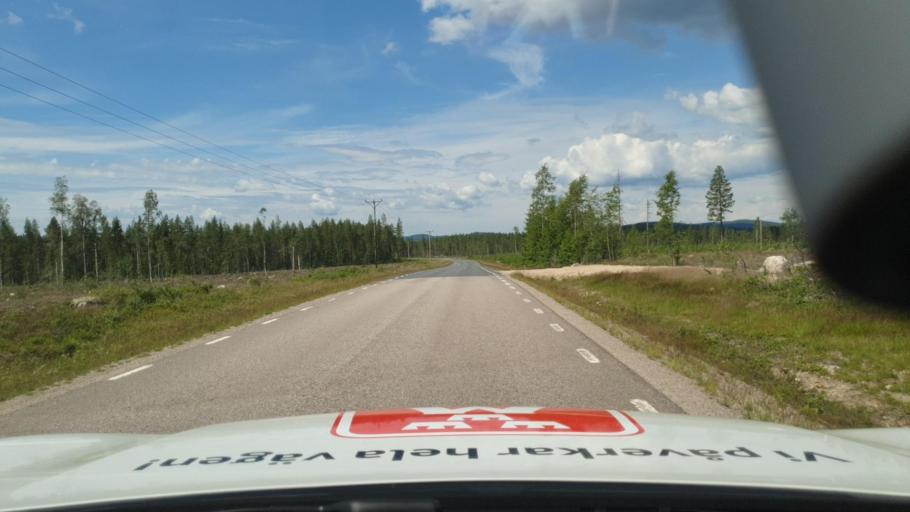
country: SE
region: Vaermland
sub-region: Torsby Kommun
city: Torsby
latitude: 60.5059
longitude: 12.8502
